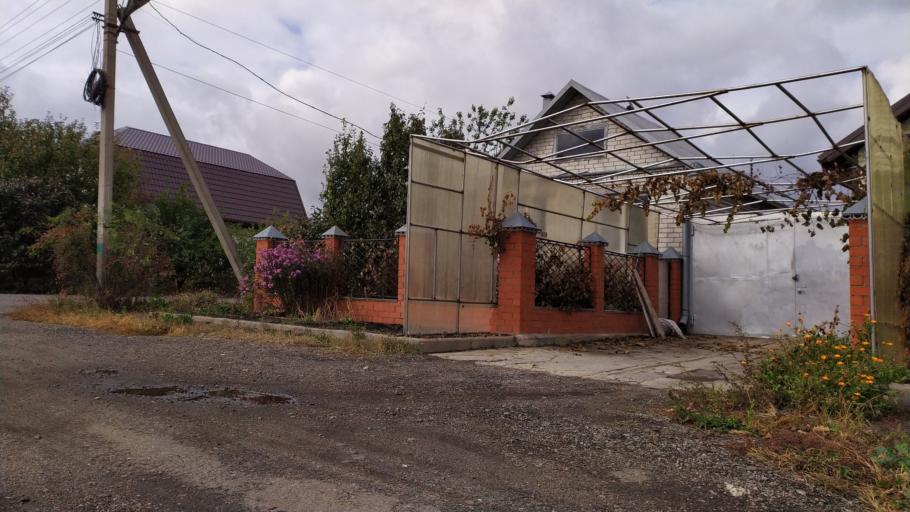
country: RU
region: Kursk
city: Kursk
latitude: 51.6417
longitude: 36.1546
